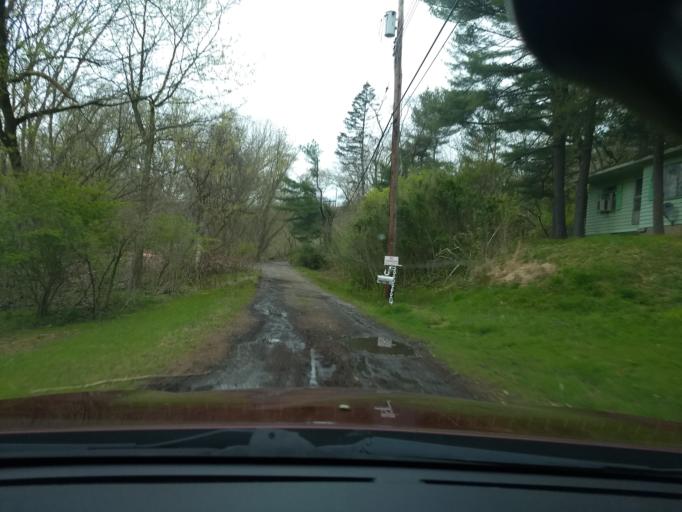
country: US
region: Pennsylvania
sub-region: Allegheny County
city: McKees Rocks
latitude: 40.4606
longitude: -80.0869
